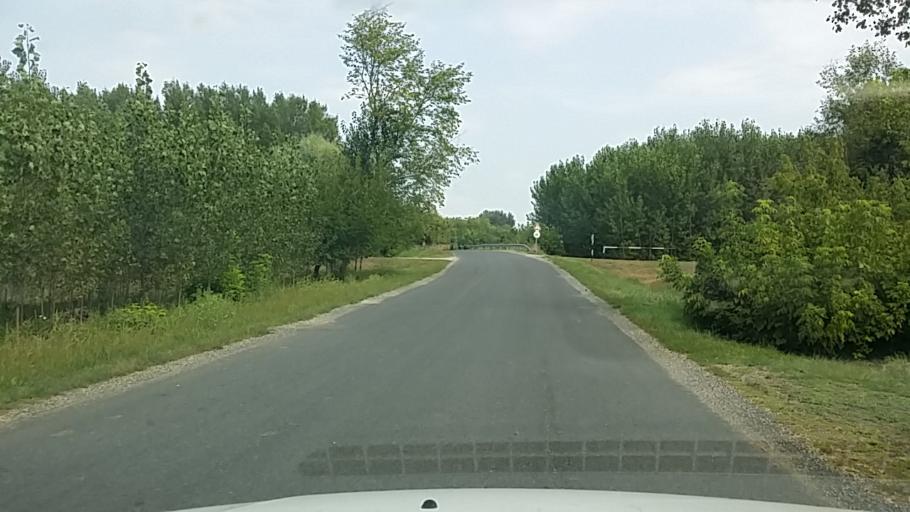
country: HU
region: Gyor-Moson-Sopron
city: Bosarkany
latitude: 47.7236
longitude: 17.3113
